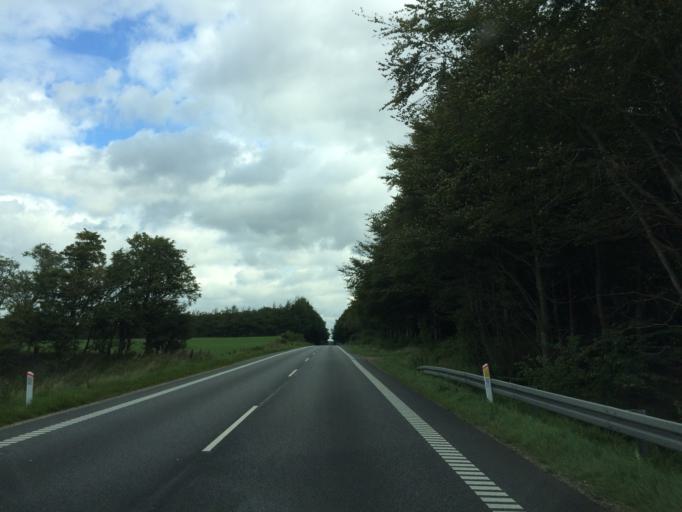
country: DK
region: Central Jutland
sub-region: Viborg Kommune
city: Stoholm
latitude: 56.4255
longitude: 9.0742
